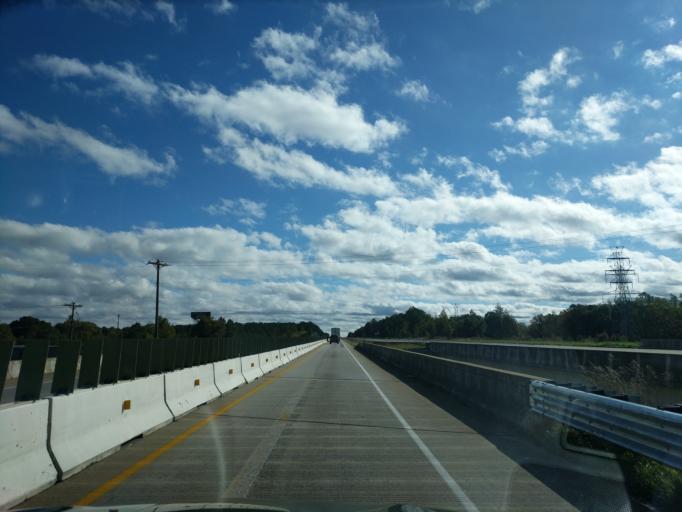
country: US
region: South Carolina
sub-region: Spartanburg County
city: Valley Falls
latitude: 35.0128
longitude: -81.9522
